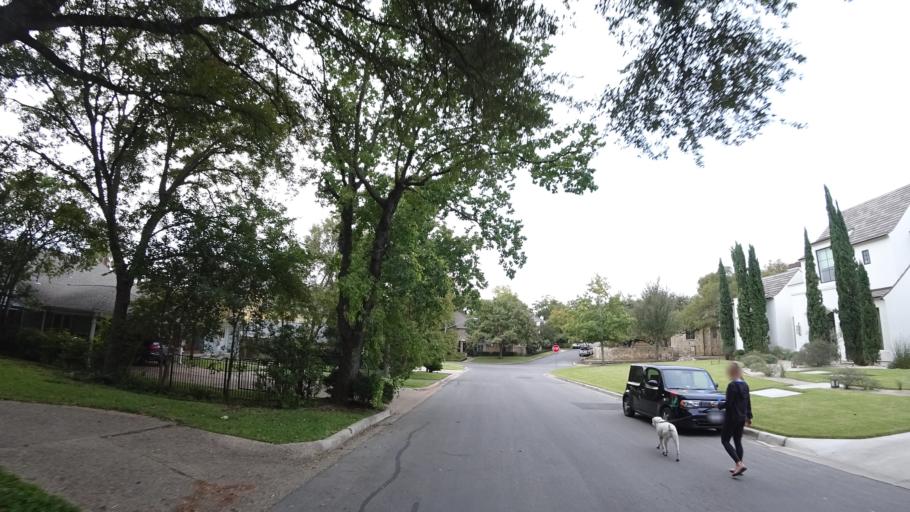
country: US
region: Texas
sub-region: Travis County
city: Austin
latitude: 30.2953
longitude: -97.7518
